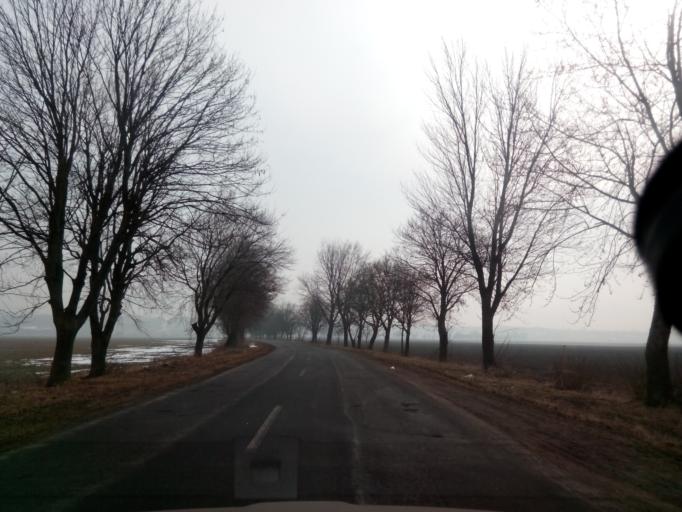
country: HU
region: Borsod-Abauj-Zemplen
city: Gonc
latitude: 48.4942
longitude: 21.2429
